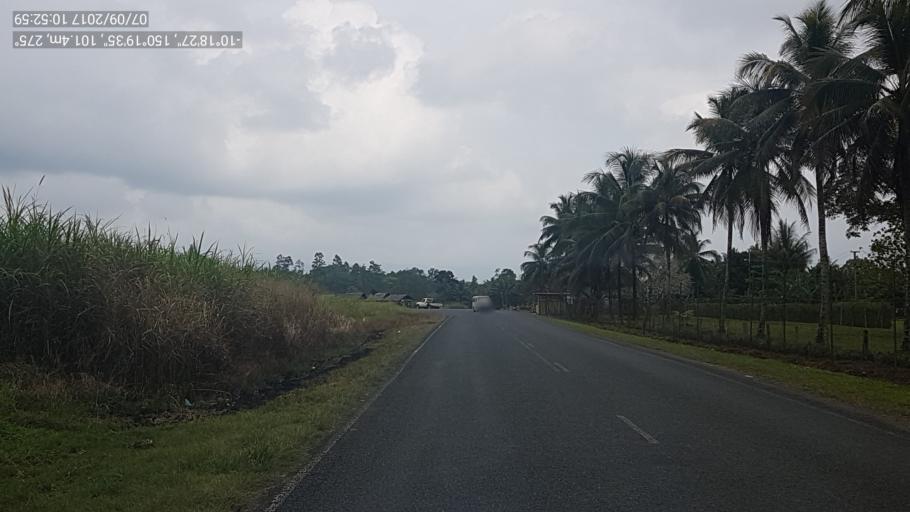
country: PG
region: Milne Bay
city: Alotau
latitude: -10.3075
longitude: 150.3264
